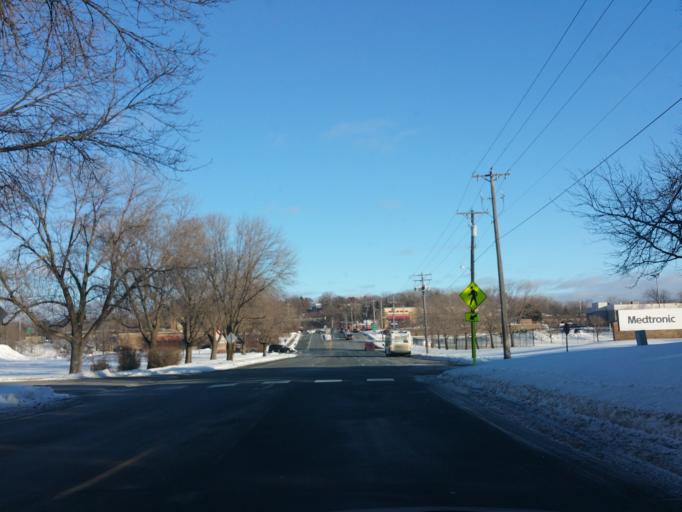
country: US
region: Minnesota
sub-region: Anoka County
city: Fridley
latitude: 45.0644
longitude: -93.2518
